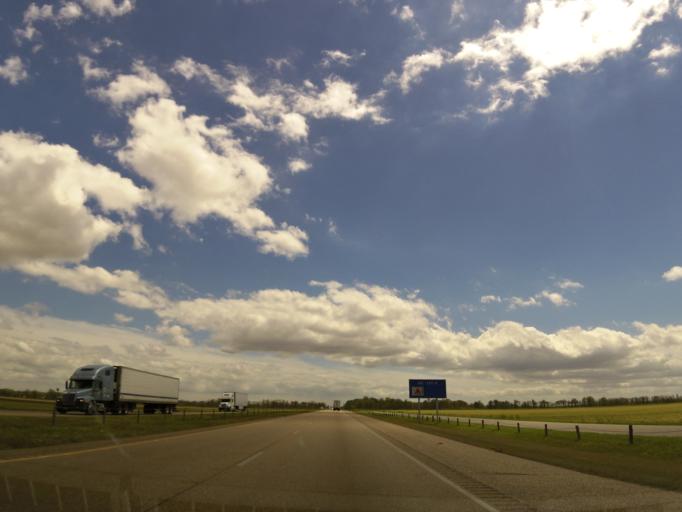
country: US
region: Arkansas
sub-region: Crittenden County
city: Marion
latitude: 35.2838
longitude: -90.2393
